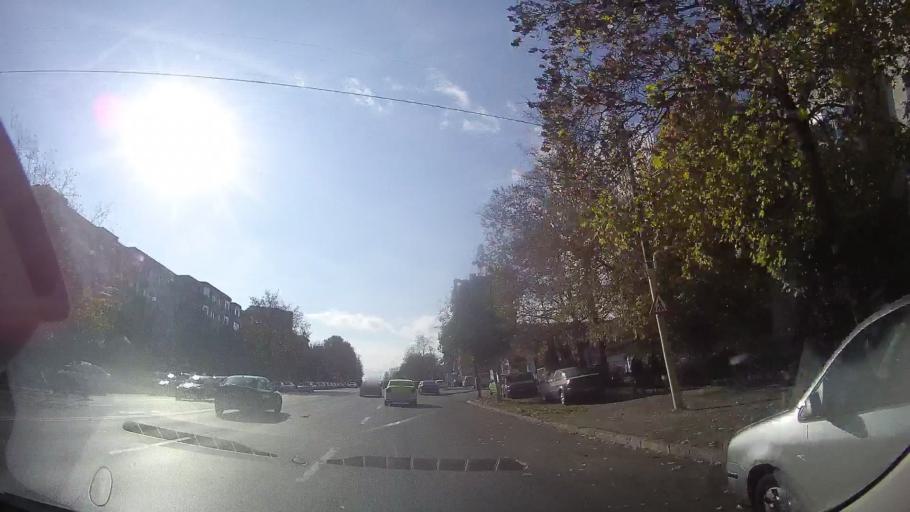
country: RO
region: Constanta
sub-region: Municipiul Constanta
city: Constanta
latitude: 44.1564
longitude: 28.6303
